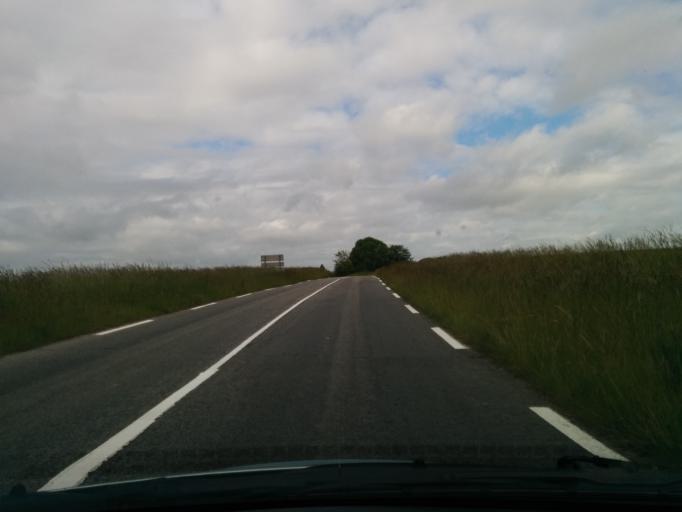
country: FR
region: Ile-de-France
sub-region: Departement des Yvelines
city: Follainville-Dennemont
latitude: 49.0158
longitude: 1.6858
